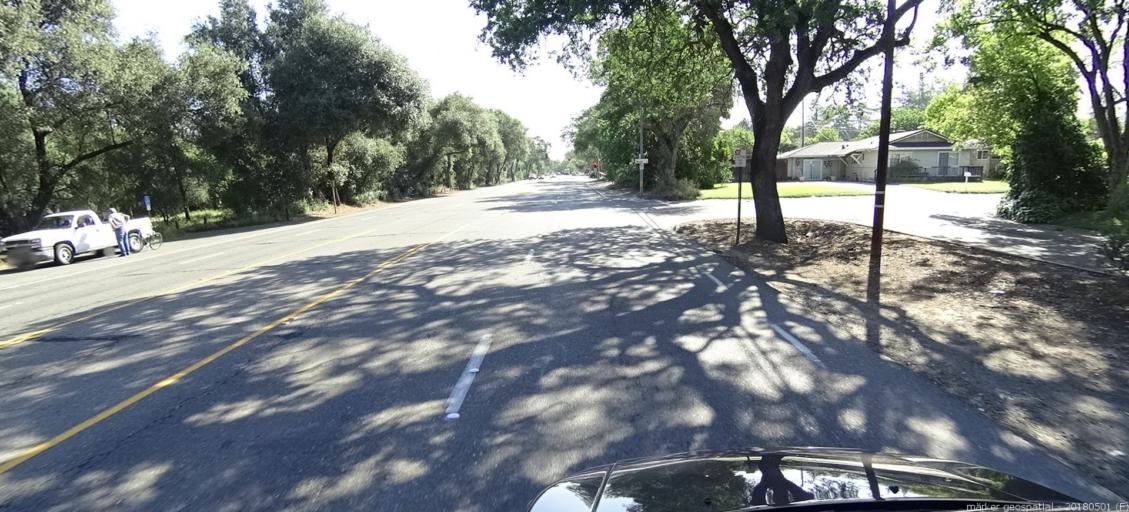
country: US
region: California
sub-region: Sacramento County
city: Arden-Arcade
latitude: 38.6411
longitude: -121.3715
